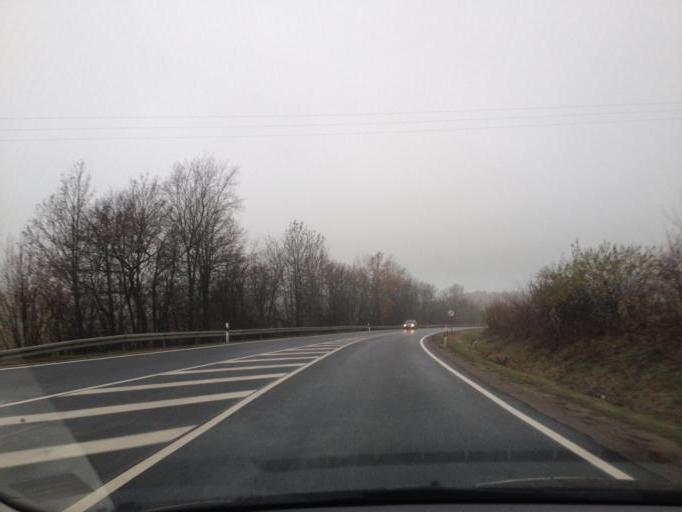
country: DE
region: Bavaria
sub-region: Regierungsbezirk Mittelfranken
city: Heroldsberg
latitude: 49.5575
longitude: 11.1749
